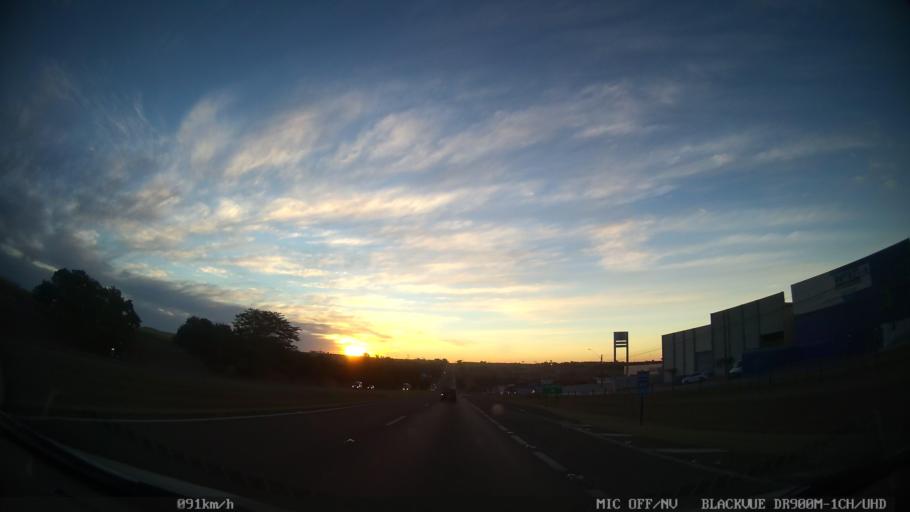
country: BR
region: Sao Paulo
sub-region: Catanduva
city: Catanduva
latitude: -21.1472
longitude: -49.0029
